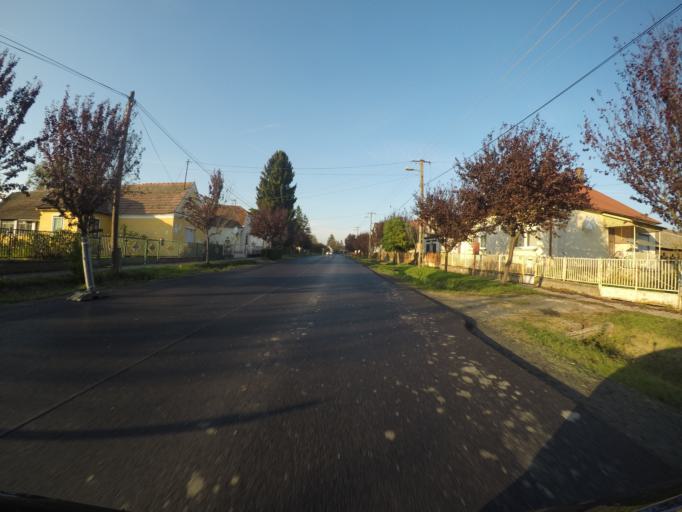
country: HU
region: Somogy
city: Barcs
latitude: 45.9841
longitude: 17.5903
